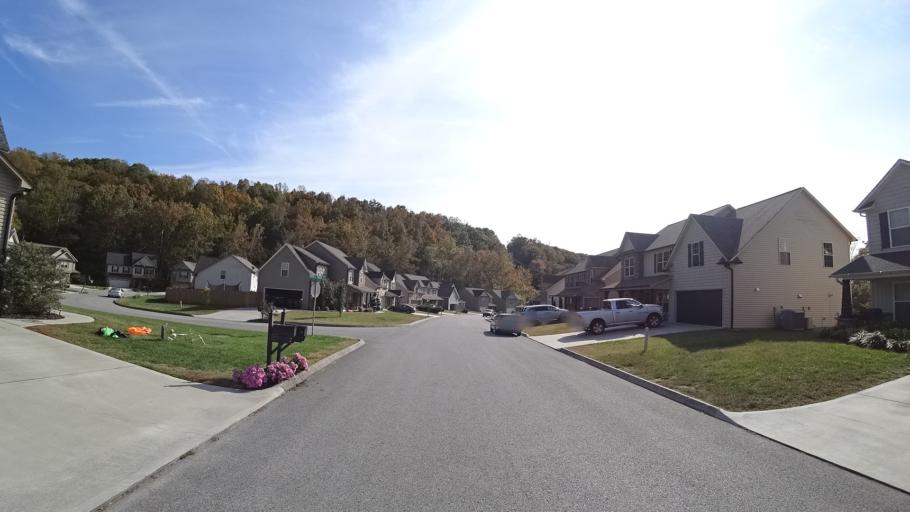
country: US
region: Tennessee
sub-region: Knox County
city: Farragut
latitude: 35.9271
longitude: -84.1595
